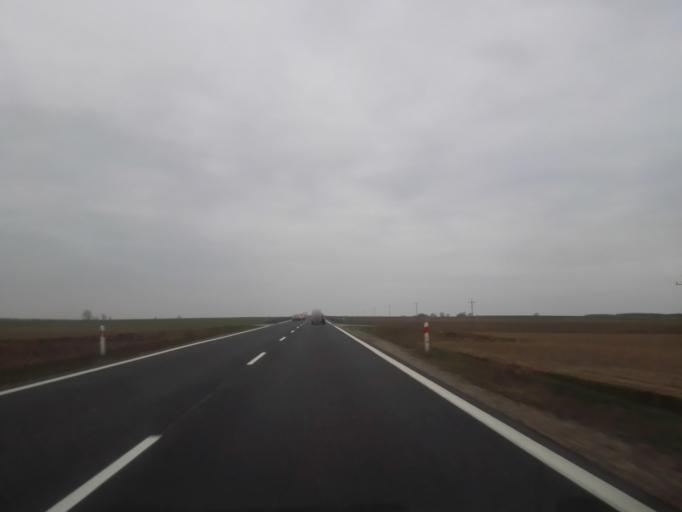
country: PL
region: Podlasie
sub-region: Powiat kolnenski
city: Stawiski
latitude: 53.4148
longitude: 22.1636
